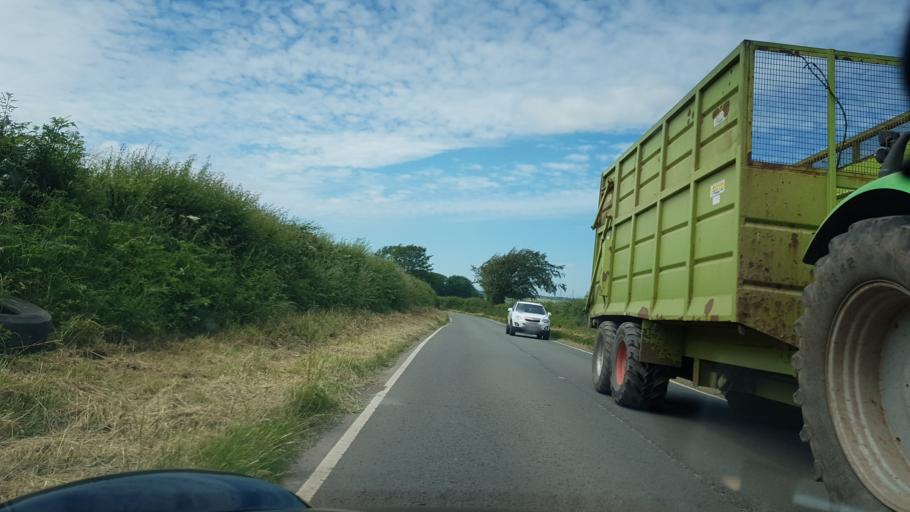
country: GB
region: Wales
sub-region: Carmarthenshire
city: Llanddowror
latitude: 51.7648
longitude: -4.5590
